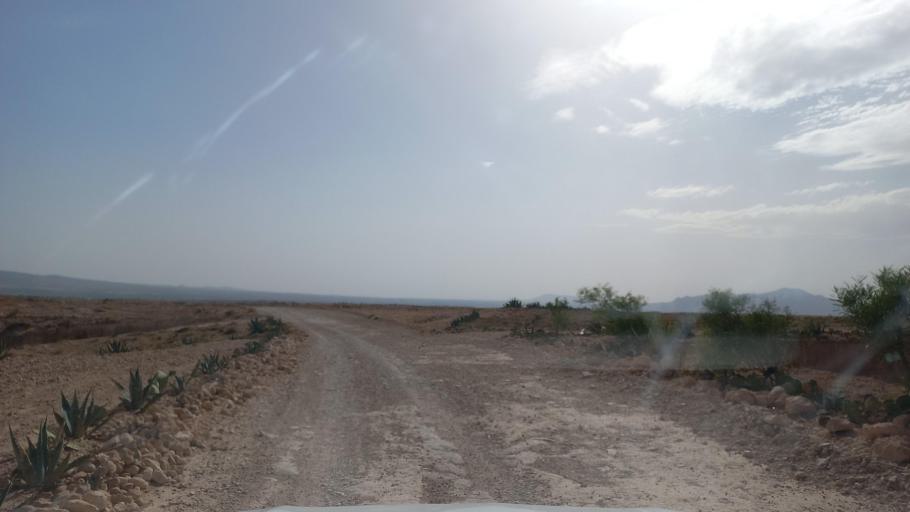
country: TN
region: Al Qasrayn
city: Kasserine
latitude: 35.2610
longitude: 8.9253
